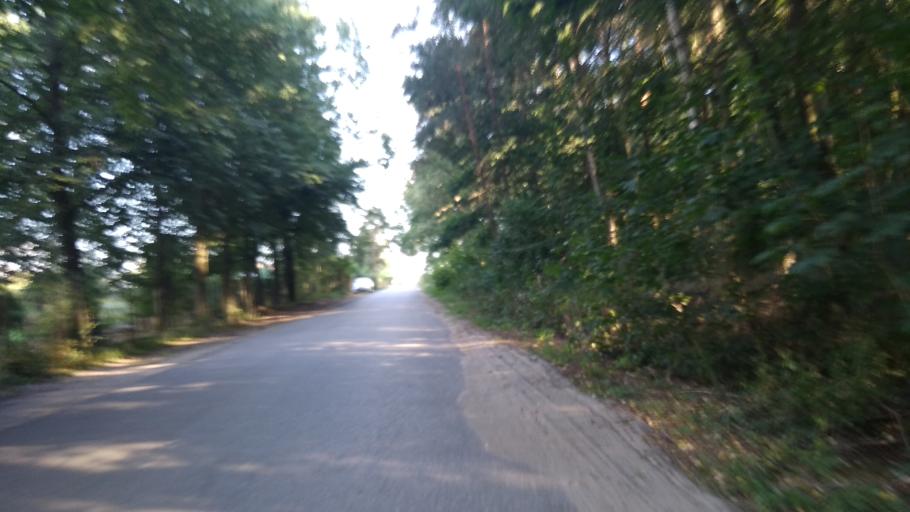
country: PL
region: Kujawsko-Pomorskie
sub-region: Powiat bydgoski
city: Osielsko
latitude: 53.2268
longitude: 18.1231
